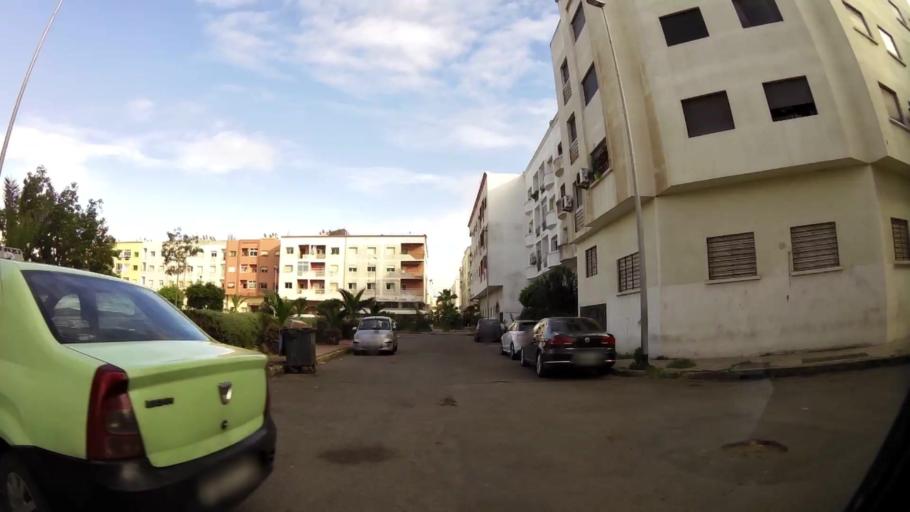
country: MA
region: Grand Casablanca
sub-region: Mohammedia
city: Mohammedia
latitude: 33.7002
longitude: -7.3972
